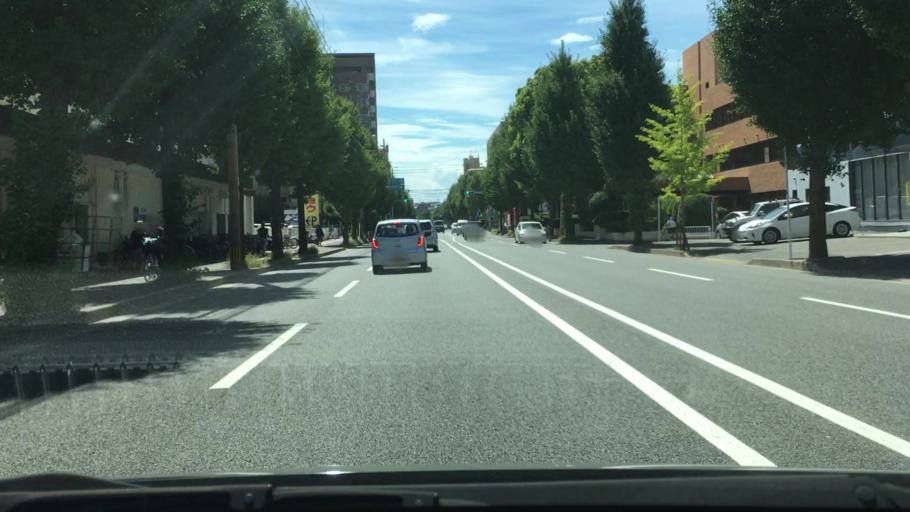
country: JP
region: Fukuoka
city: Fukuoka-shi
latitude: 33.5691
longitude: 130.4254
